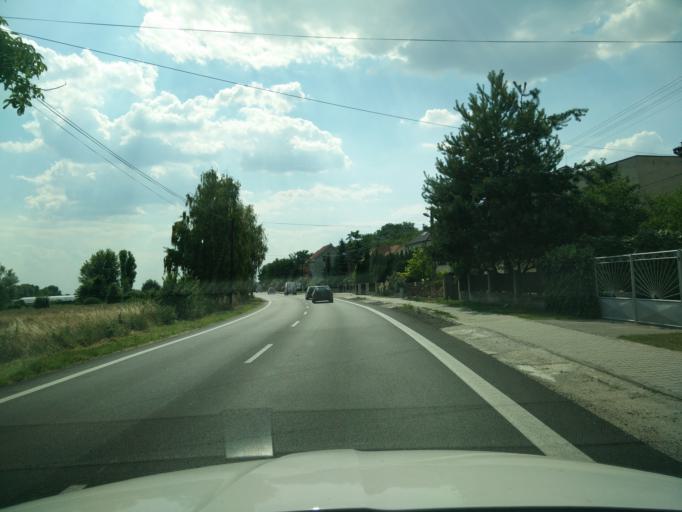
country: SK
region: Nitriansky
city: Partizanske
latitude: 48.6305
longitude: 18.3451
